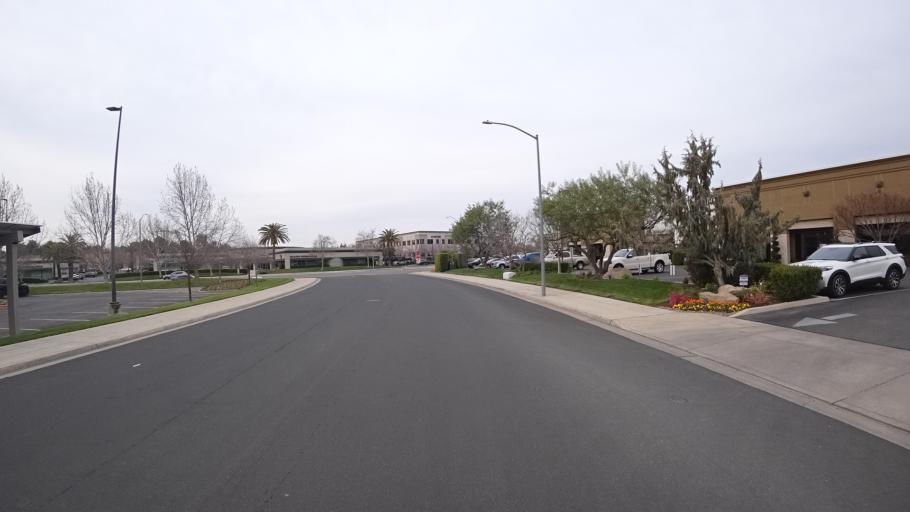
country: US
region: California
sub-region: Fresno County
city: Fresno
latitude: 36.8457
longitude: -119.8078
